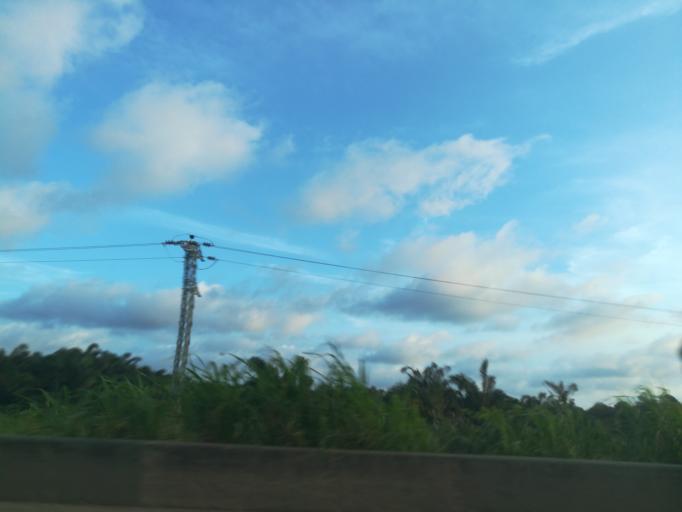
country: NG
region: Lagos
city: Badagry
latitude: 6.4734
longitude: 3.0097
